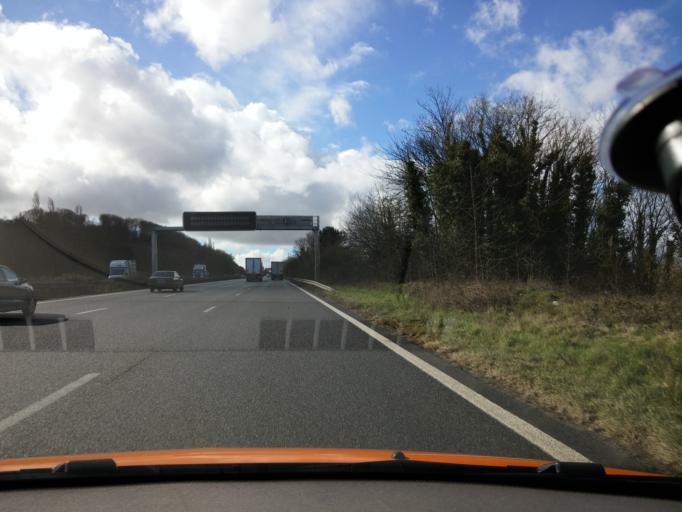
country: FR
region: Ile-de-France
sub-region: Departement de l'Essonne
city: Villebon-sur-Yvette
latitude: 48.6980
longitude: 2.2412
